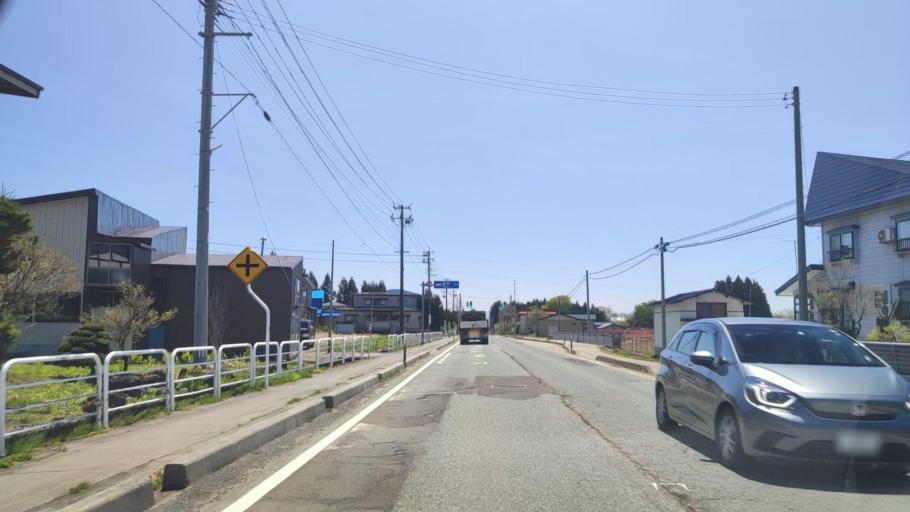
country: JP
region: Yamagata
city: Shinjo
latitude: 38.8278
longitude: 140.3276
